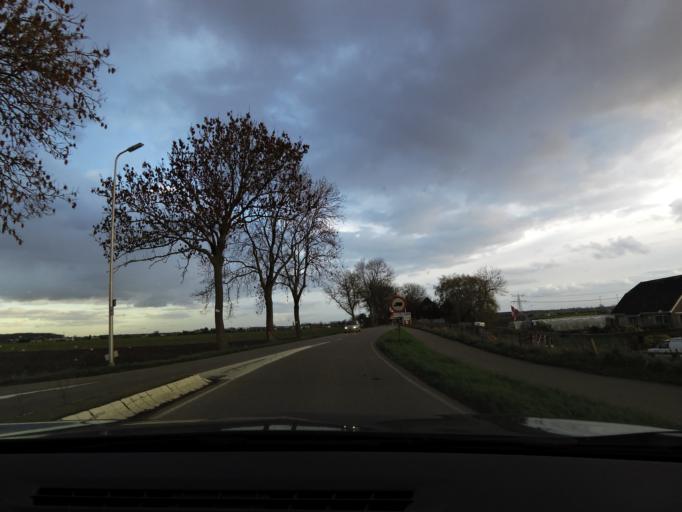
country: NL
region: South Holland
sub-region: Gemeente Binnenmaas
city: Mijnsheerenland
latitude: 51.8172
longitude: 4.4989
